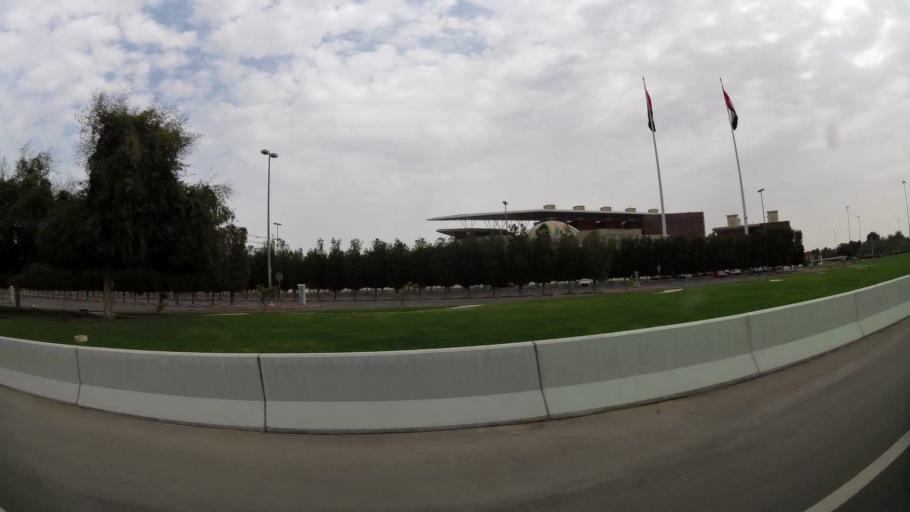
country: AE
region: Abu Dhabi
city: Abu Dhabi
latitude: 24.4174
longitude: 54.4438
